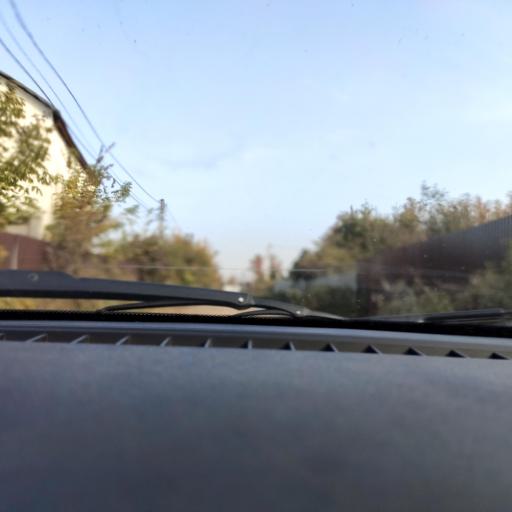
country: RU
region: Bashkortostan
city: Ufa
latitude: 54.6893
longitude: 55.8924
